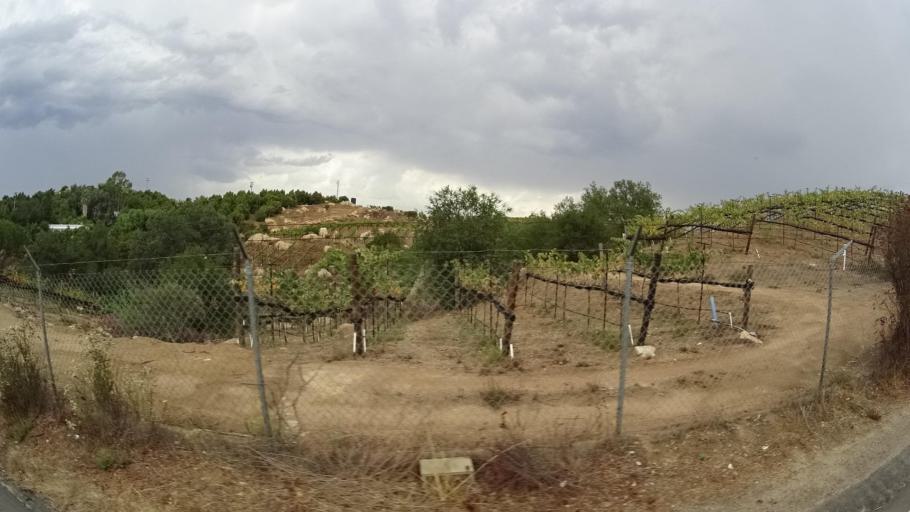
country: US
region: California
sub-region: San Diego County
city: San Pasqual
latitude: 33.0602
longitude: -116.9757
